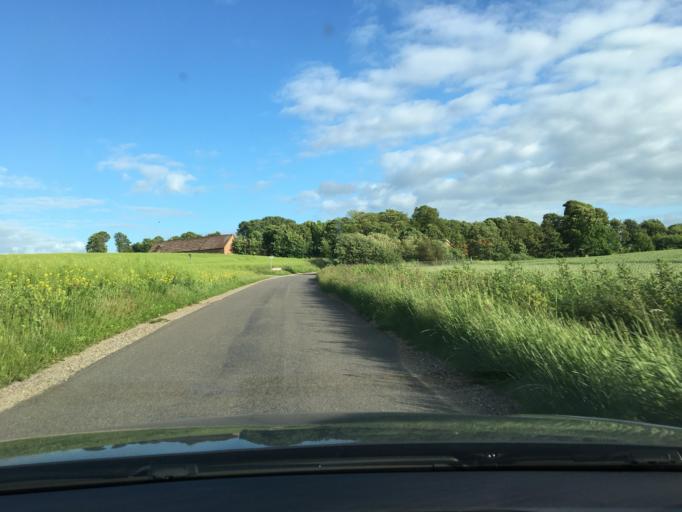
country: DK
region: Central Jutland
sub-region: Favrskov Kommune
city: Hinnerup
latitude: 56.3007
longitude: 10.1059
